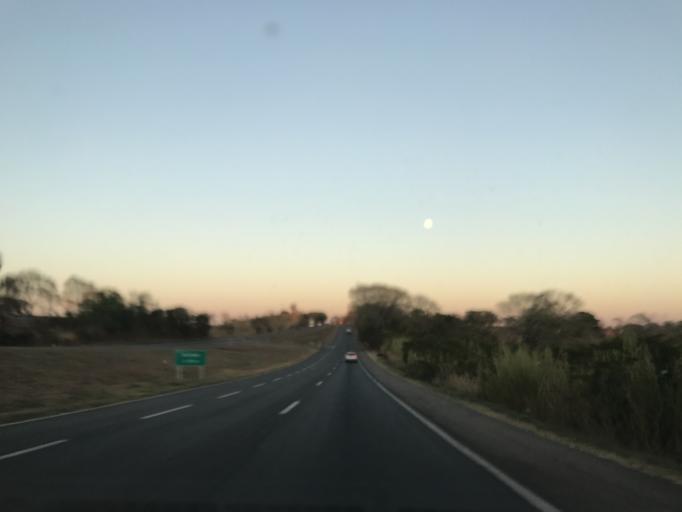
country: BR
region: Goias
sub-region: Abadiania
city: Abadiania
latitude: -16.1621
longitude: -48.6235
